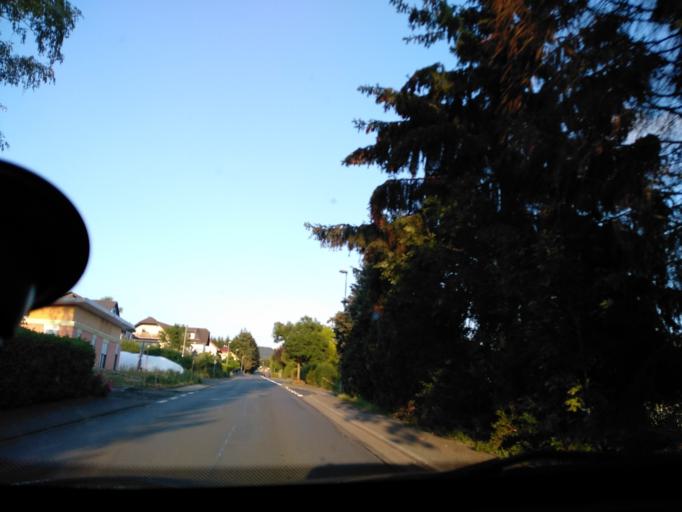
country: DE
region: Hesse
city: Dillenburg
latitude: 50.8151
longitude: 8.3444
